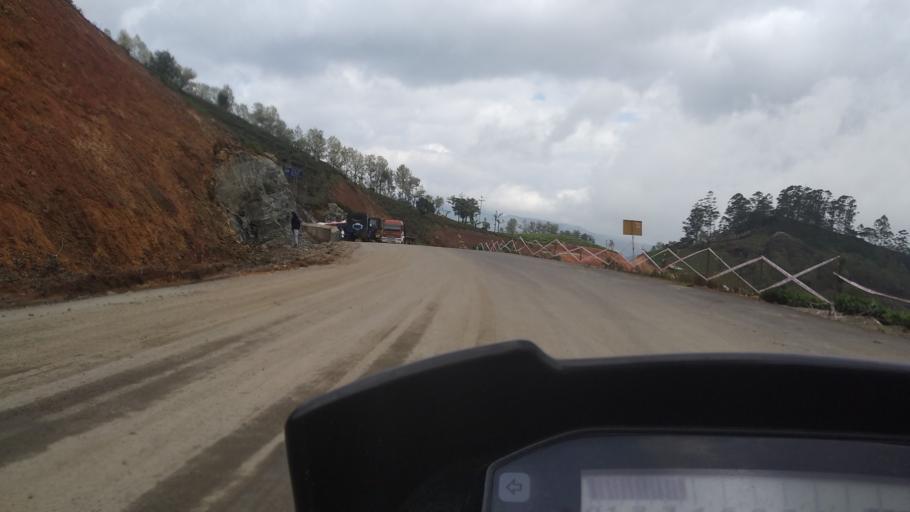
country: IN
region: Kerala
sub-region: Idukki
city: Munnar
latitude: 10.0377
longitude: 77.1545
